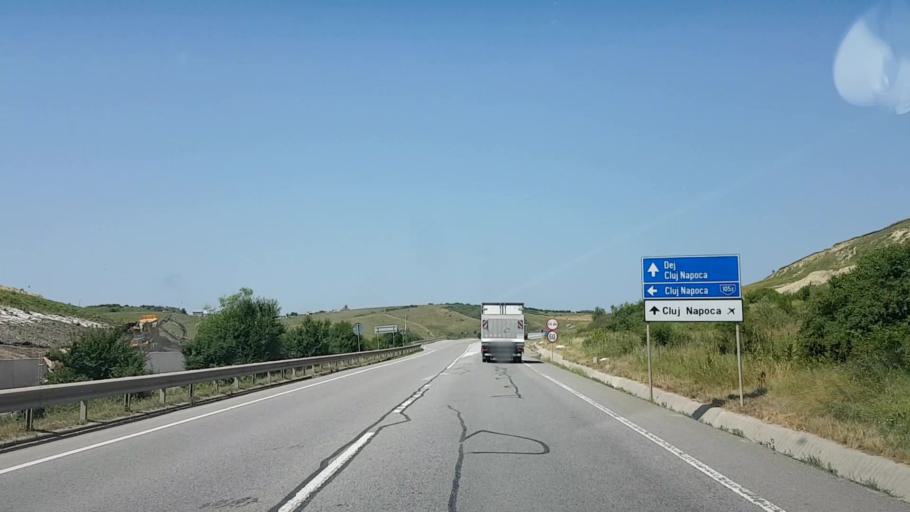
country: RO
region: Cluj
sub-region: Comuna Apahida
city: Dezmir
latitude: 46.7655
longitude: 23.6903
